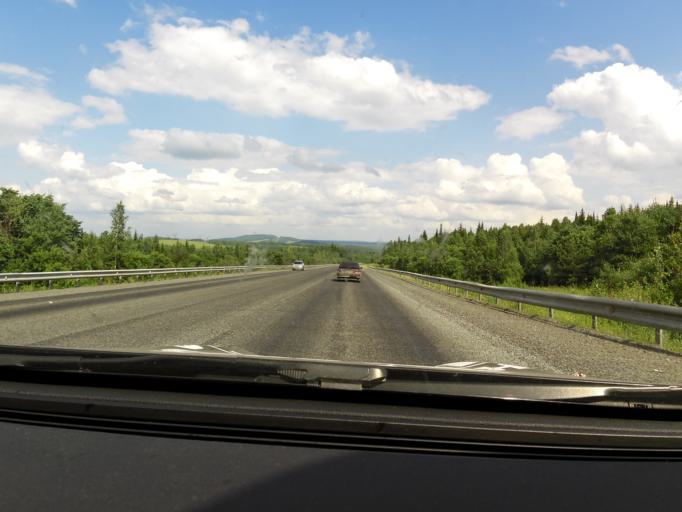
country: RU
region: Sverdlovsk
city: Arti
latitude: 56.7880
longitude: 58.5557
